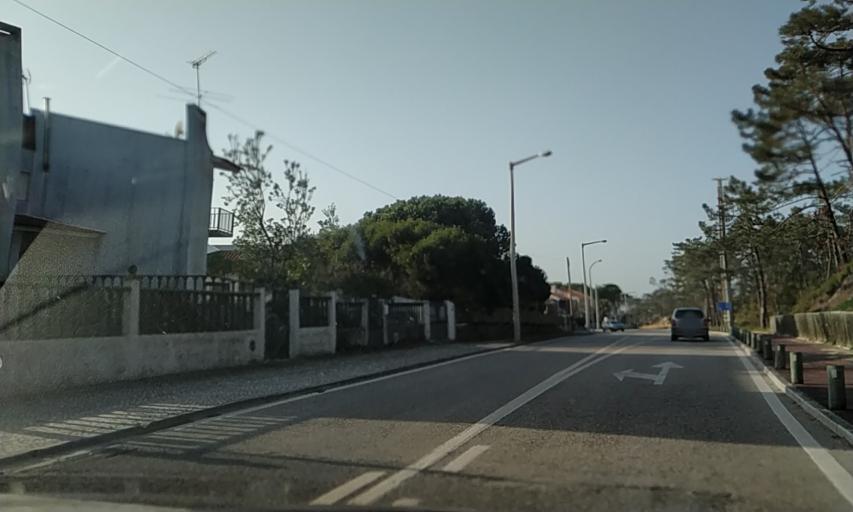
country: PT
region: Leiria
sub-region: Alcobaca
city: Pataias
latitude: 39.7545
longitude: -9.0242
